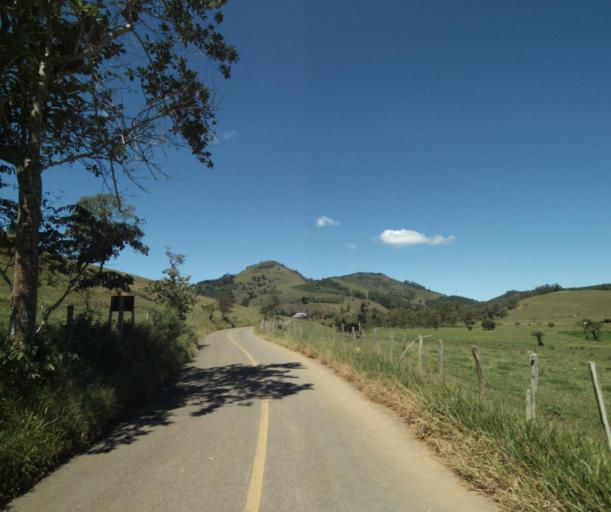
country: BR
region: Minas Gerais
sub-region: Espera Feliz
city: Espera Feliz
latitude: -20.6198
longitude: -41.8355
